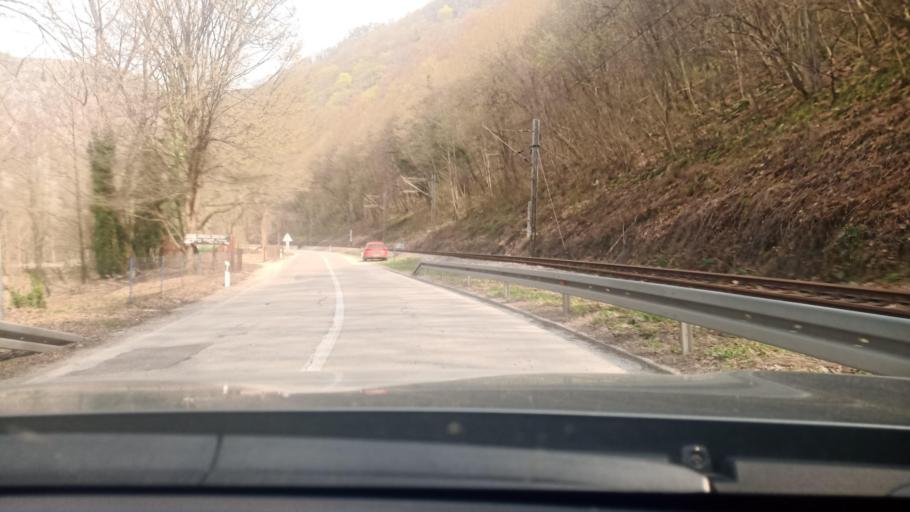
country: BA
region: Federation of Bosnia and Herzegovina
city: Stijena
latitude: 44.9007
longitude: 16.0052
